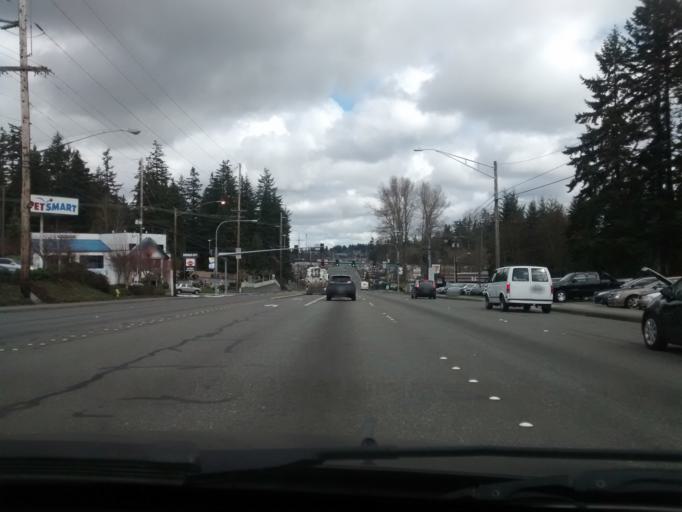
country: US
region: Washington
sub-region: Snohomish County
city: Lynnwood
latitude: 47.8274
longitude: -122.3097
